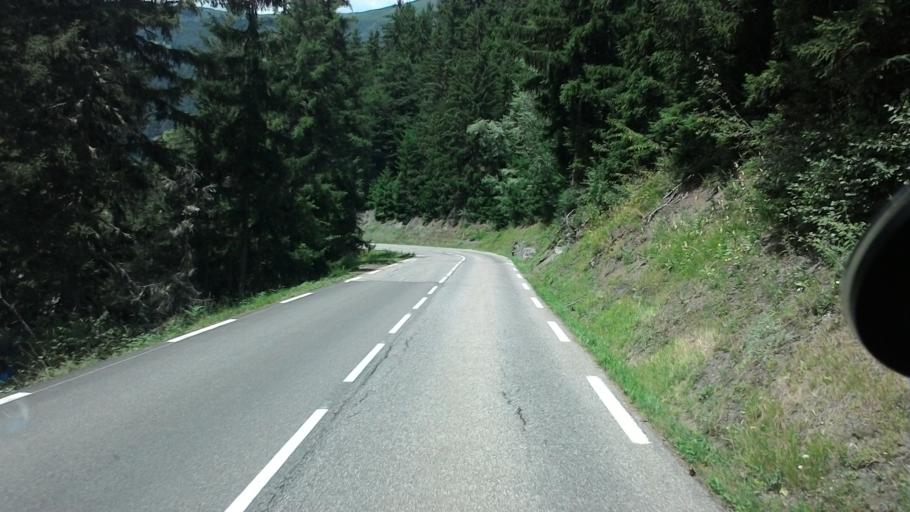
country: FR
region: Rhone-Alpes
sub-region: Departement de la Savoie
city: Seez
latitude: 45.6282
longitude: 6.8240
